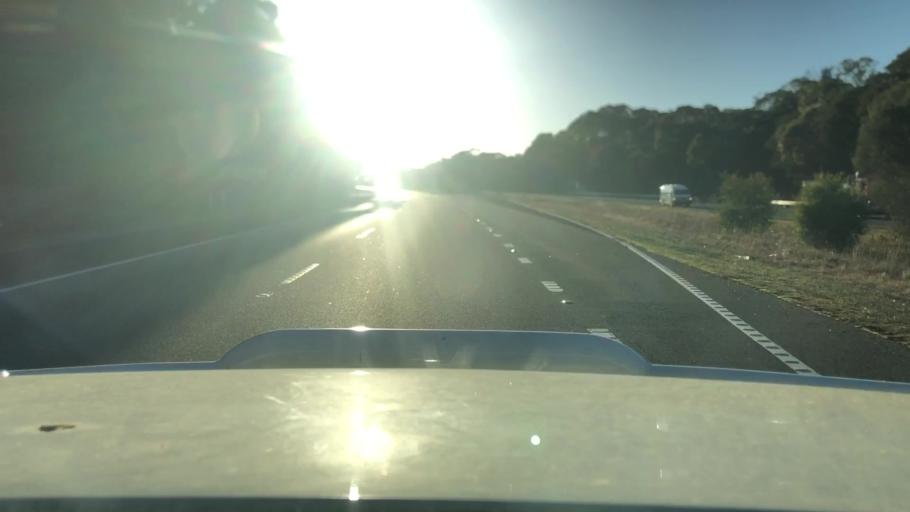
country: AU
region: New South Wales
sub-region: Wingecarribee
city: Bundanoon
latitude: -34.6356
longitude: 150.1444
